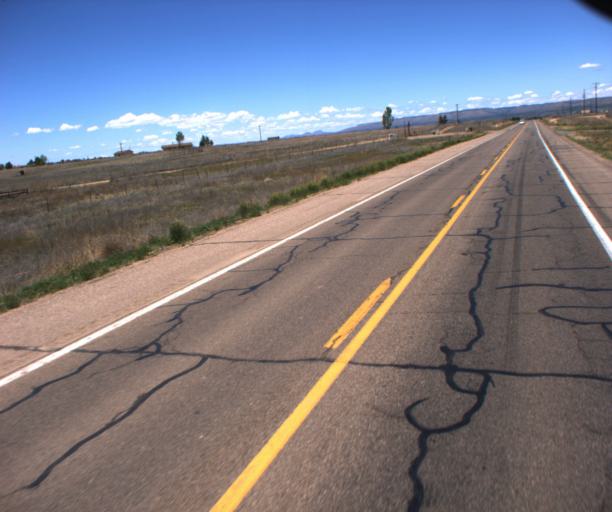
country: US
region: Arizona
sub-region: Yavapai County
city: Paulden
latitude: 34.8451
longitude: -112.4654
